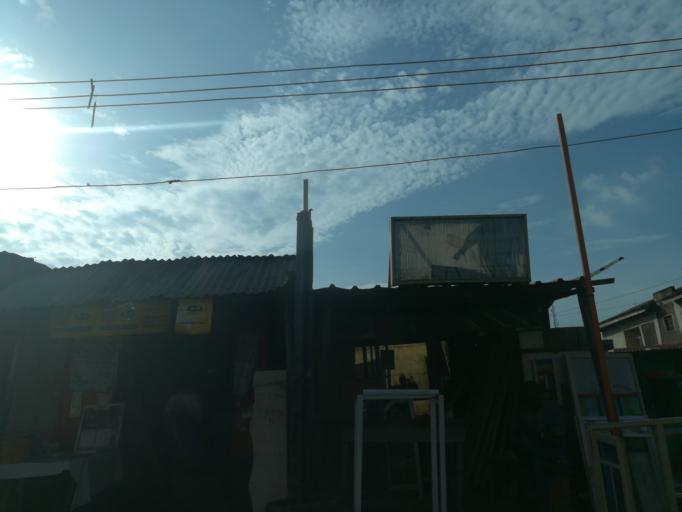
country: NG
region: Lagos
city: Ojota
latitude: 6.6064
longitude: 3.4211
